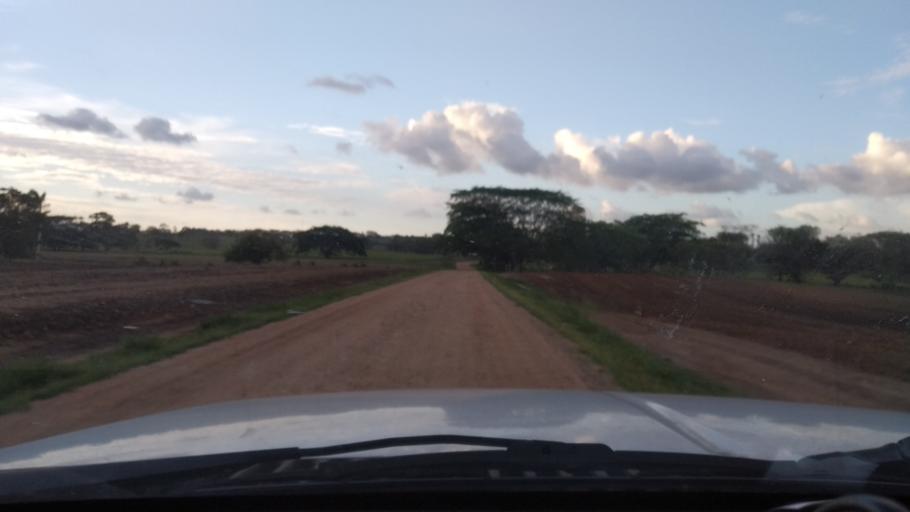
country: BZ
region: Cayo
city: San Ignacio
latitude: 17.2206
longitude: -88.9984
